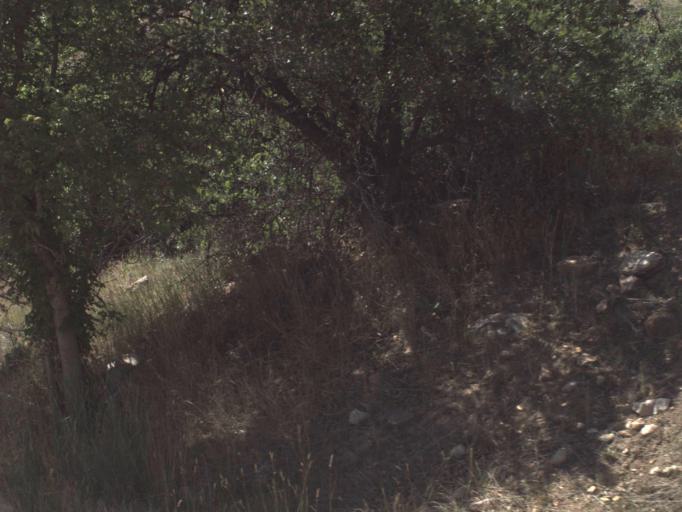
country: US
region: Utah
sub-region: Weber County
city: Wolf Creek
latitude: 41.2670
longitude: -111.6808
